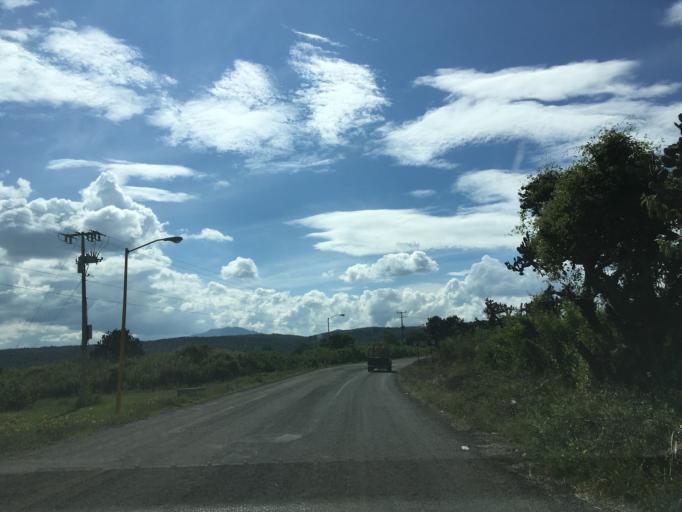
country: MX
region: Michoacan
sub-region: Jimenez
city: Villa Jimenez
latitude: 19.9017
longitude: -101.7700
